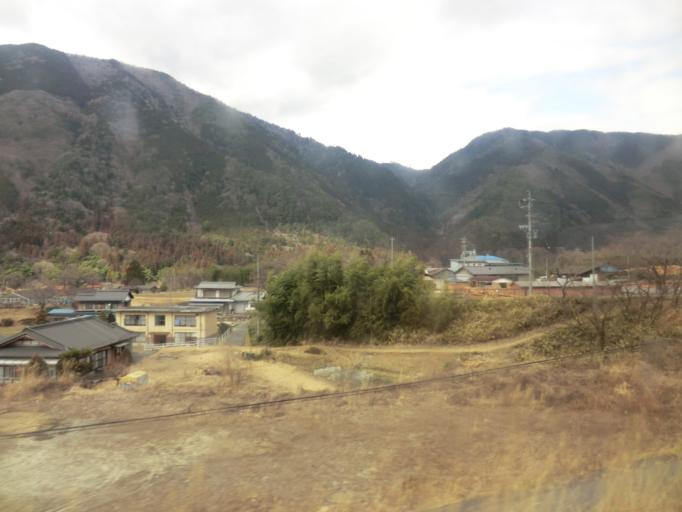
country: JP
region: Gifu
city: Nakatsugawa
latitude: 35.6714
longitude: 137.6335
